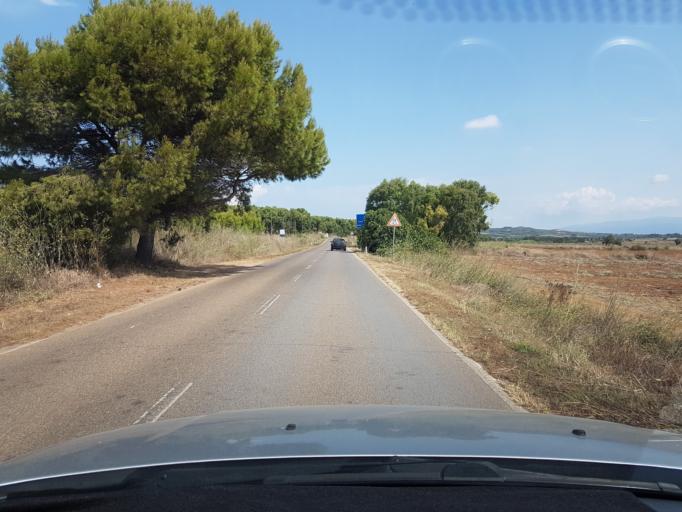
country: IT
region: Sardinia
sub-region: Provincia di Oristano
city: Cabras
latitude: 39.8958
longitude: 8.4347
